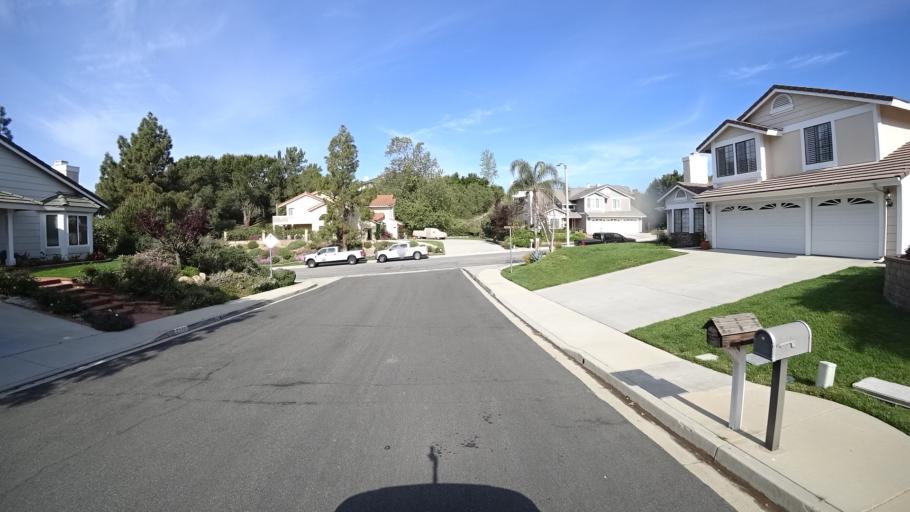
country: US
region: California
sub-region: Ventura County
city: Thousand Oaks
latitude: 34.2154
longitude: -118.8305
